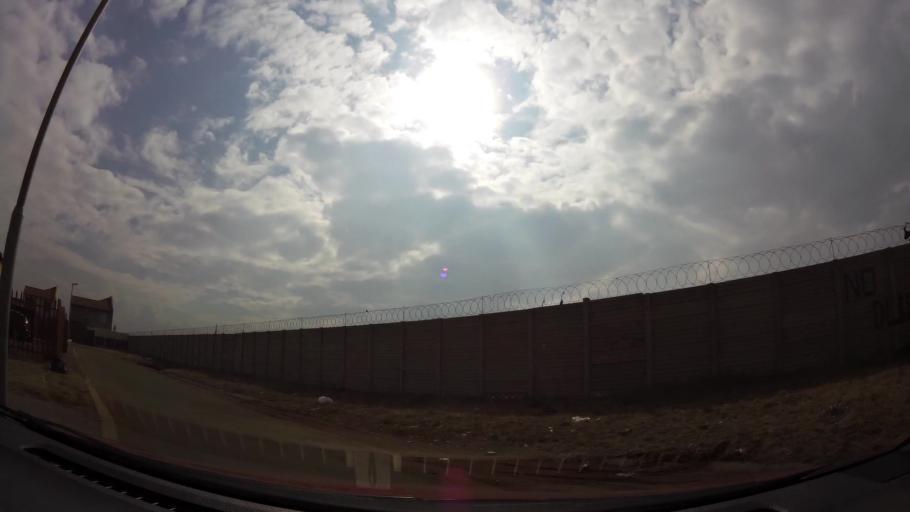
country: ZA
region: Gauteng
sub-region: Sedibeng District Municipality
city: Vanderbijlpark
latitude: -26.6792
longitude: 27.8412
